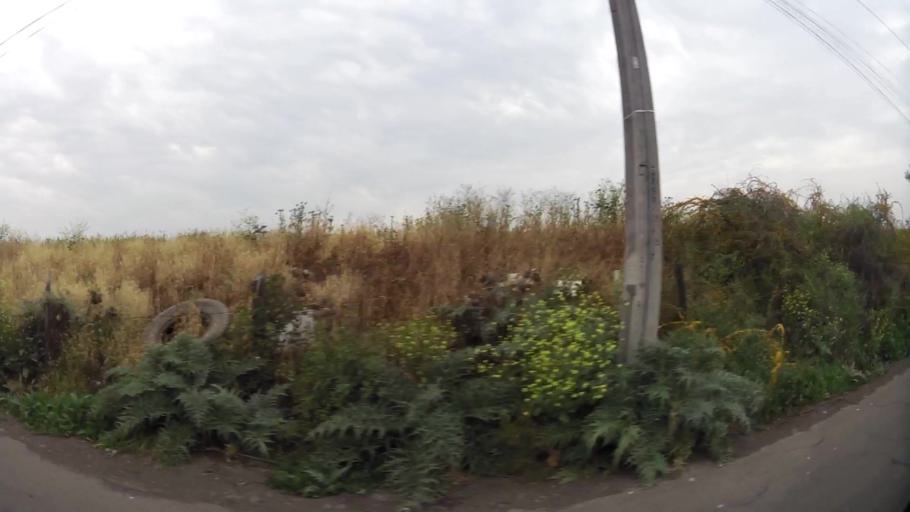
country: CL
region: Santiago Metropolitan
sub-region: Provincia de Chacabuco
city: Chicureo Abajo
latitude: -33.2615
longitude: -70.7647
